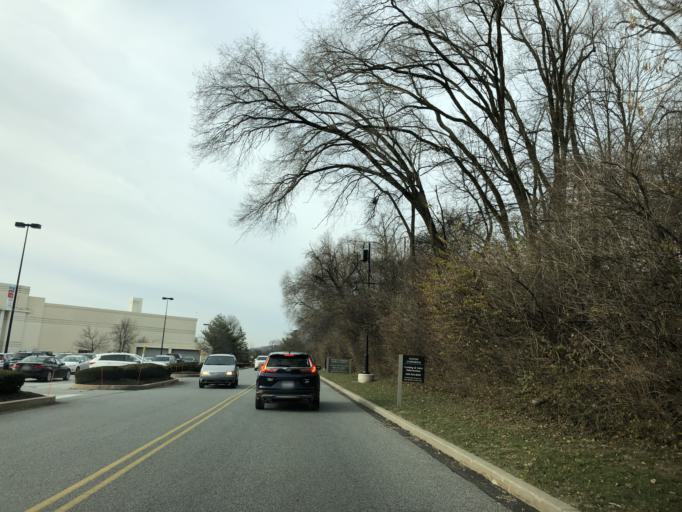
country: US
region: Pennsylvania
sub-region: Chester County
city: Exton
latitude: 40.0333
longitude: -75.6234
